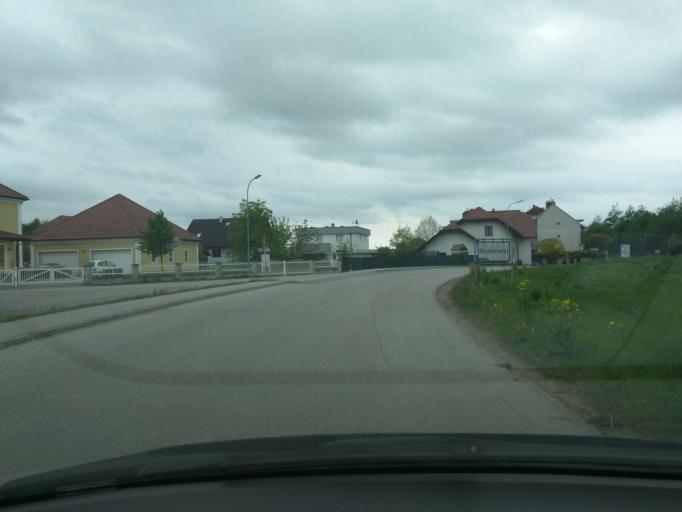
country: AT
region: Lower Austria
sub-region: Politischer Bezirk Melk
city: Blindenmarkt
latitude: 48.1247
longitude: 14.9892
